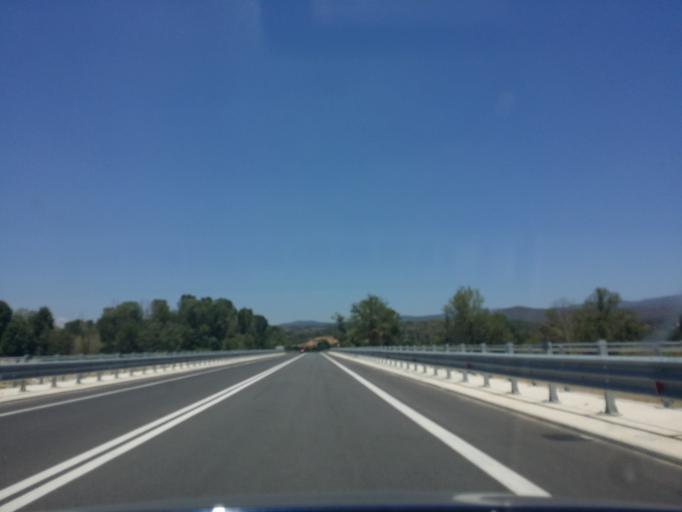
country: GR
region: Peloponnese
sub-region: Nomos Lakonias
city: Sparti
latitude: 37.0112
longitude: 22.4846
